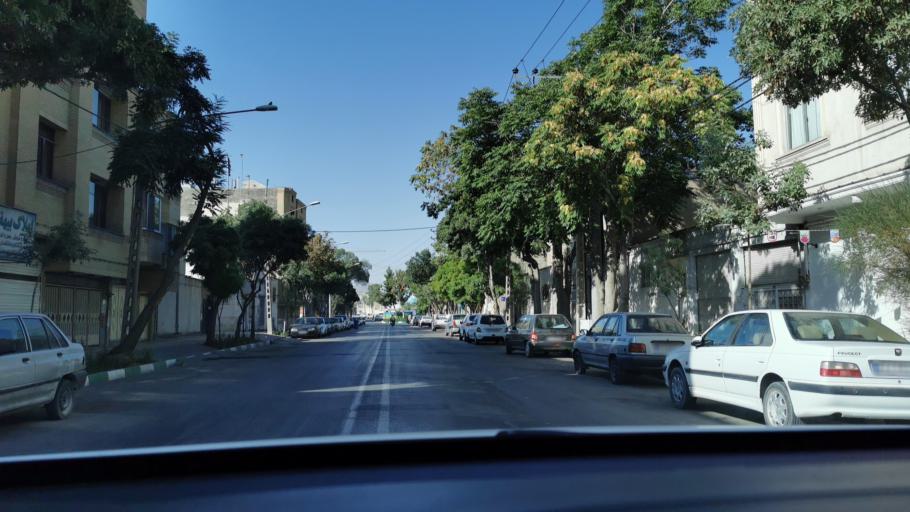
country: IR
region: Razavi Khorasan
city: Mashhad
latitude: 36.2998
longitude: 59.6205
